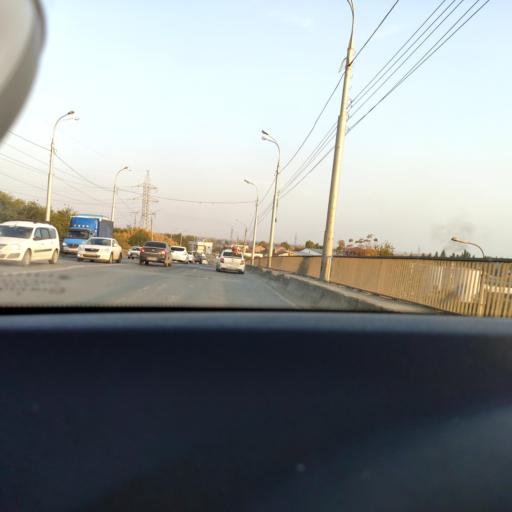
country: RU
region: Samara
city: Petra-Dubrava
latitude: 53.2551
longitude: 50.3056
